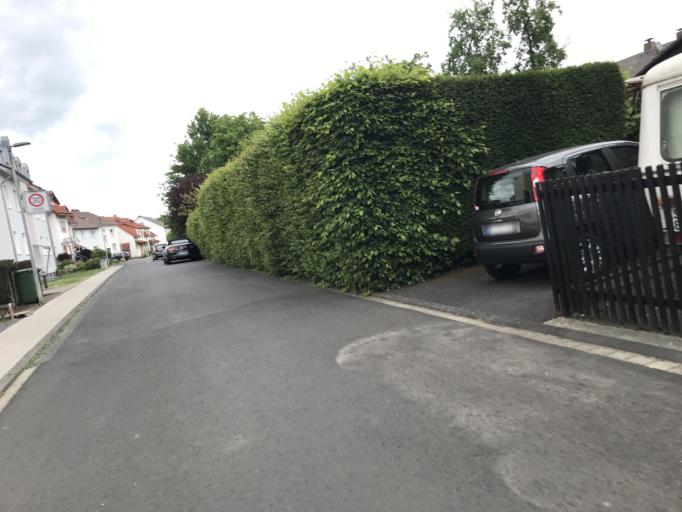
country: DE
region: Hesse
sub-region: Regierungsbezirk Kassel
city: Baunatal
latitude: 51.2475
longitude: 9.3924
